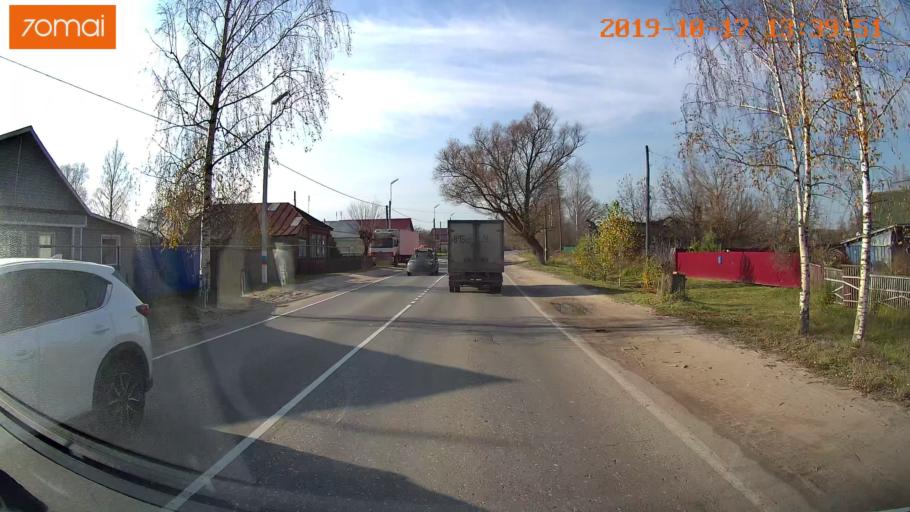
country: RU
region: Rjazan
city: Tuma
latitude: 55.1465
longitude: 40.5803
